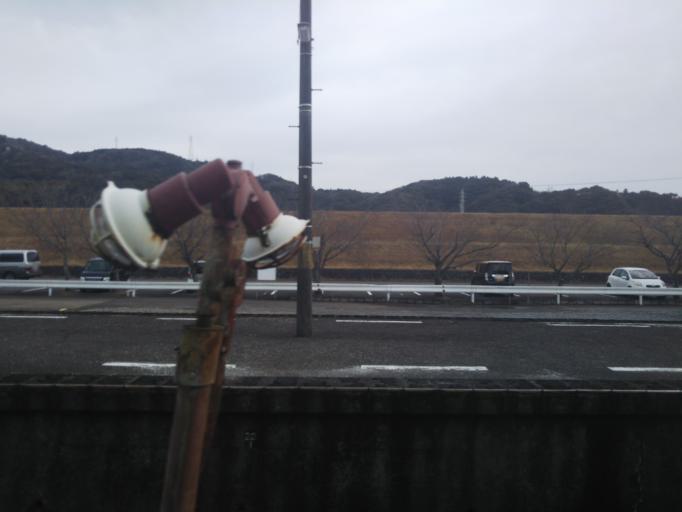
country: JP
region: Kochi
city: Nakamura
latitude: 32.9842
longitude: 132.9444
